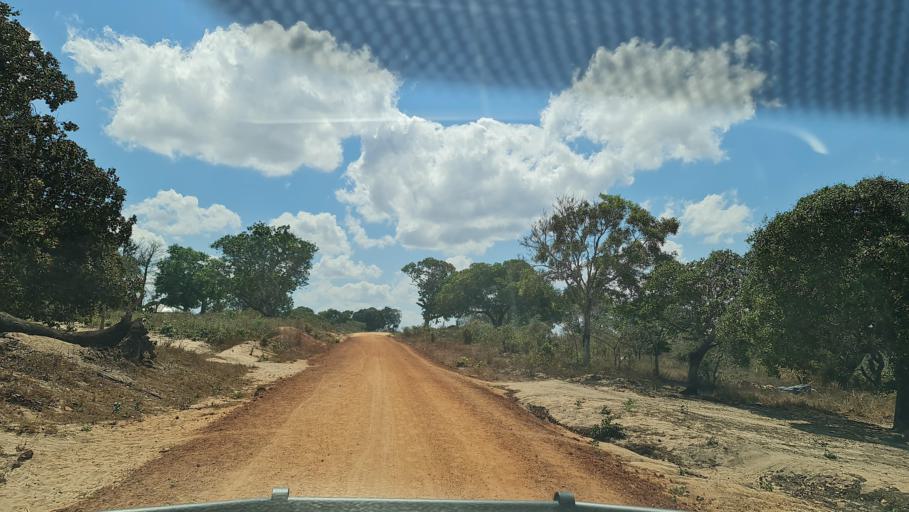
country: MZ
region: Nampula
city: Nacala
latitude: -14.1758
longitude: 40.2123
